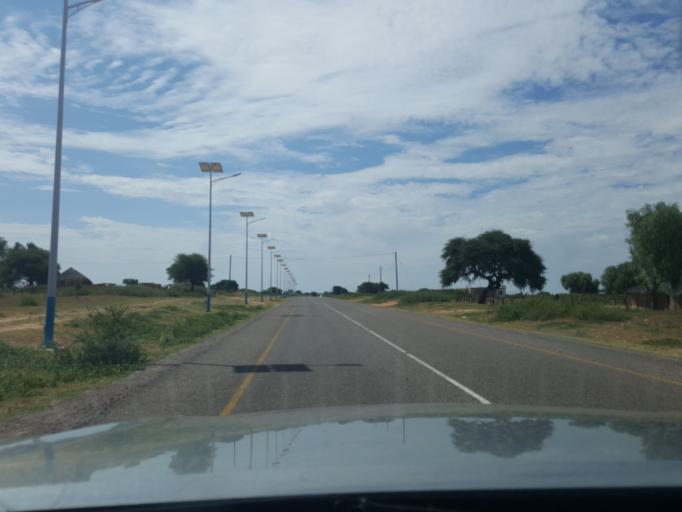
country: BW
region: Kweneng
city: Letlhakeng
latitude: -24.0827
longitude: 25.0309
